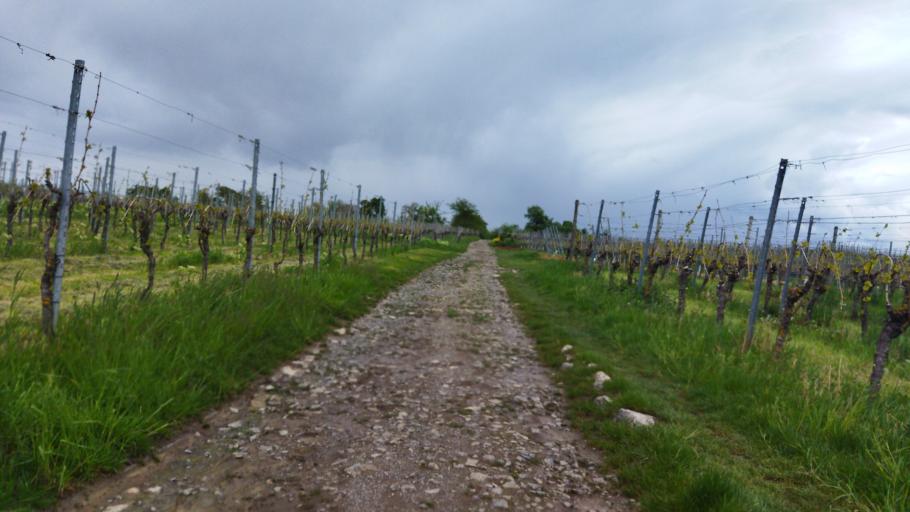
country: DE
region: Baden-Wuerttemberg
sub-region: Regierungsbezirk Stuttgart
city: Hessigheim
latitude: 49.0033
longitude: 9.1916
